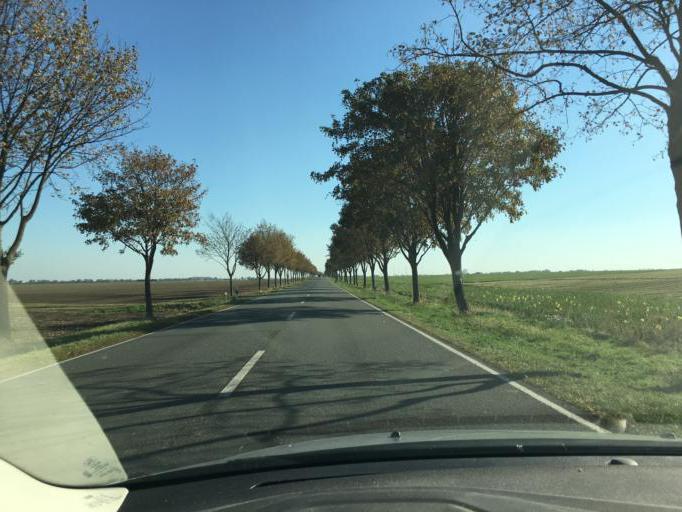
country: DE
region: Saxony-Anhalt
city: Wanzleben
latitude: 52.0236
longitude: 11.4925
